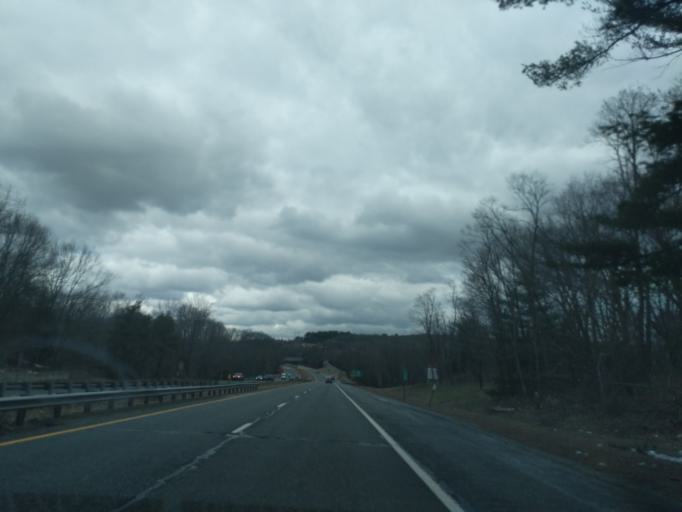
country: US
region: Massachusetts
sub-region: Worcester County
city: Blackstone
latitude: 41.9949
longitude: -71.5561
